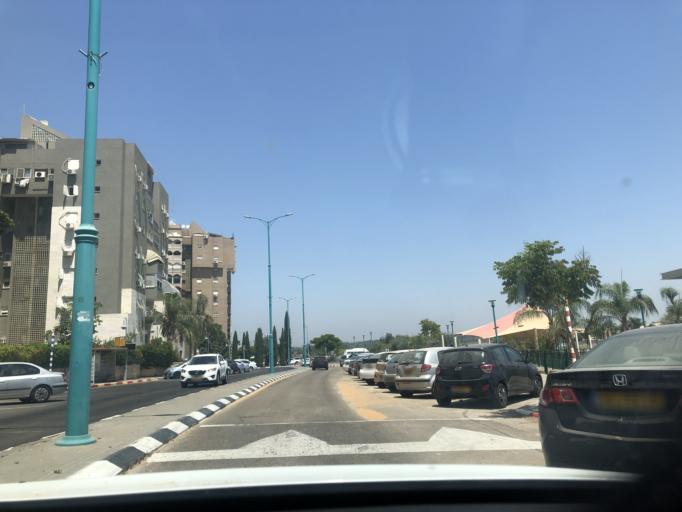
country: IL
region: Central District
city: Lod
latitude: 31.9447
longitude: 34.9043
